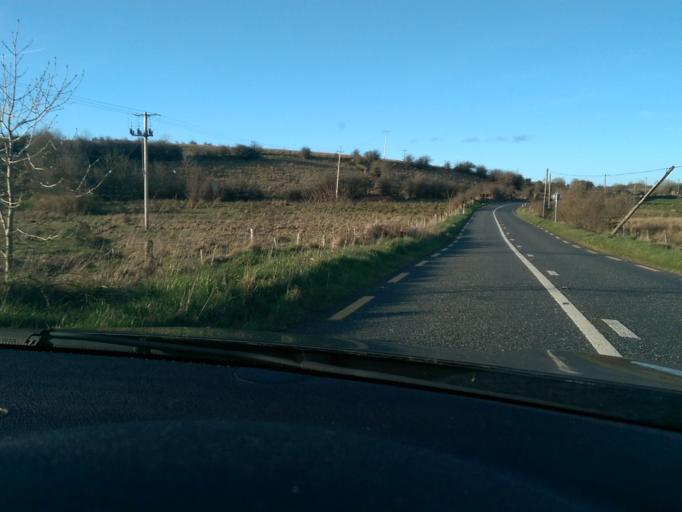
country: IE
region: Connaught
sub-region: Roscommon
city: Boyle
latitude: 53.9382
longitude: -8.2759
